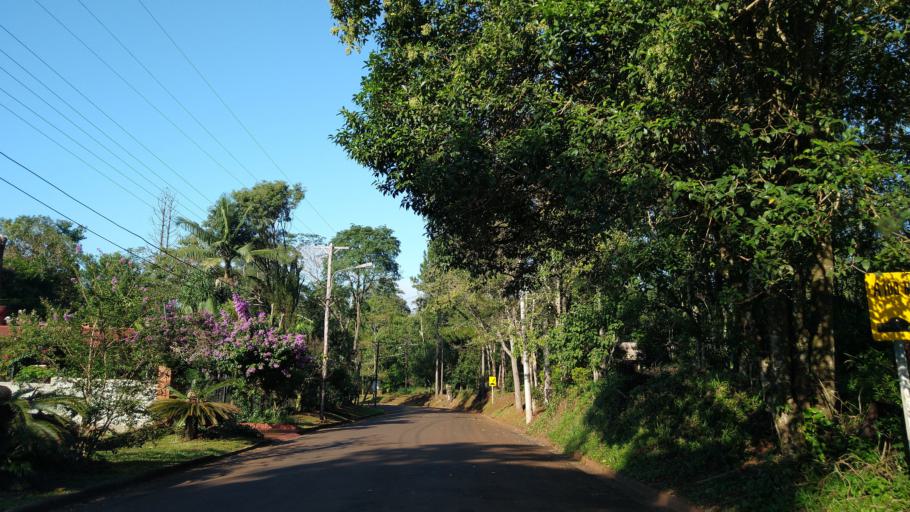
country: AR
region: Misiones
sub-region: Departamento de Montecarlo
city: Montecarlo
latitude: -26.5588
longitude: -54.7766
